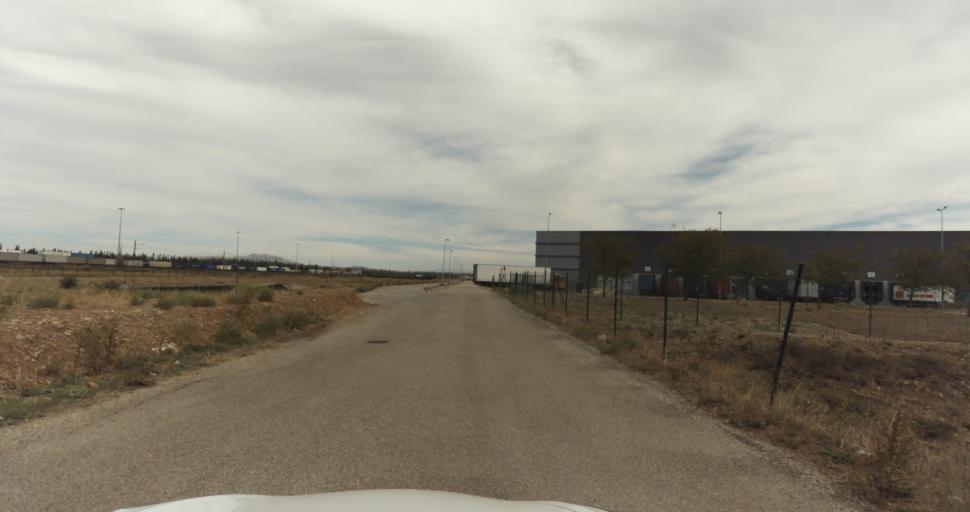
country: FR
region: Provence-Alpes-Cote d'Azur
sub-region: Departement des Bouches-du-Rhone
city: Miramas
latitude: 43.6041
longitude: 4.9907
